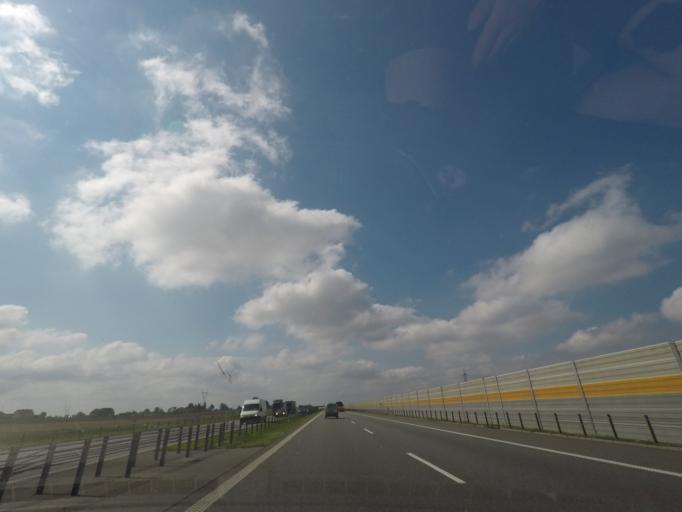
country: PL
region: Kujawsko-Pomorskie
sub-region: Powiat torunski
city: Lubicz Dolny
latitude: 53.0644
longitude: 18.7485
